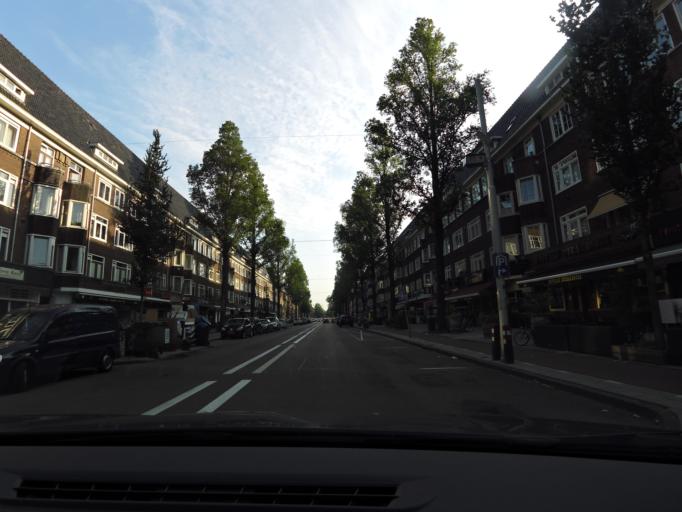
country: NL
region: North Holland
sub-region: Gemeente Amsterdam
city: Amsterdam
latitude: 52.3449
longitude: 4.8908
